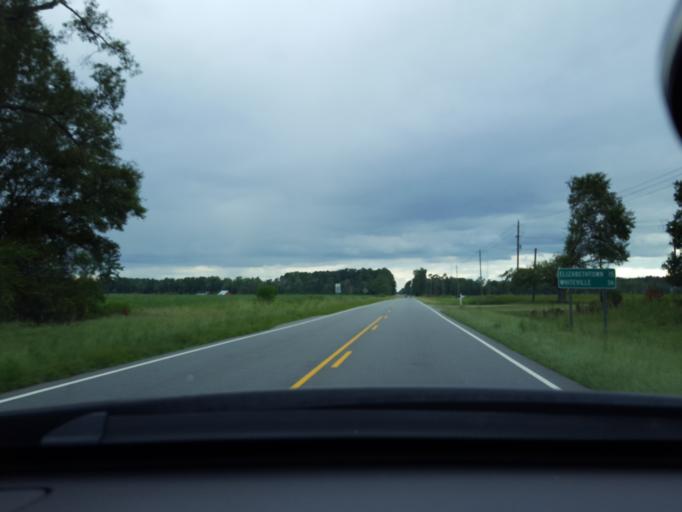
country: US
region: North Carolina
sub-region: Bladen County
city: Elizabethtown
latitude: 34.7474
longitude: -78.4224
